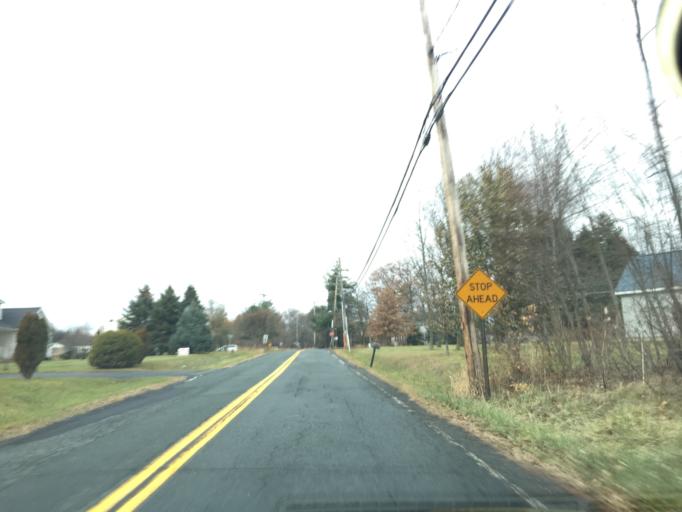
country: US
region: New York
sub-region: Rensselaer County
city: Wynantskill
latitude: 42.6664
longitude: -73.6420
